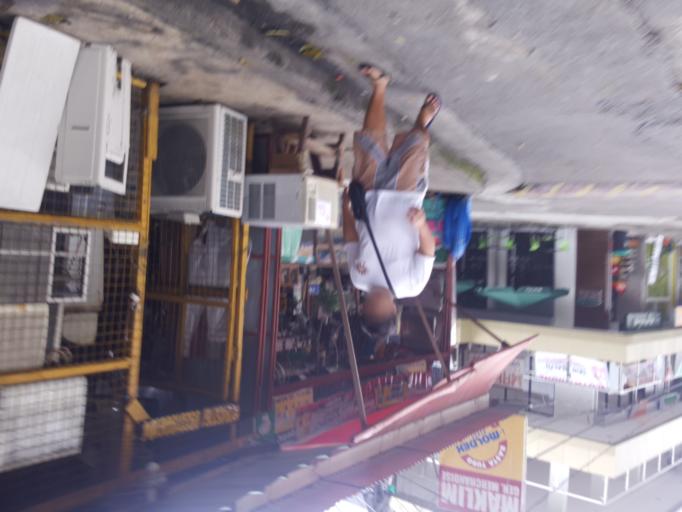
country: PH
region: Calabarzon
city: Bagong Pagasa
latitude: 14.7023
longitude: 121.0228
